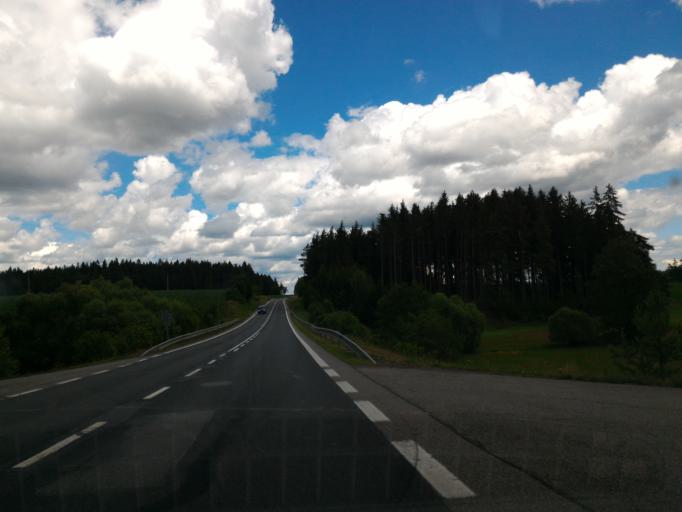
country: CZ
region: Vysocina
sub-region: Okres Zd'ar nad Sazavou
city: Nove Veseli
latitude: 49.5033
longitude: 15.8916
